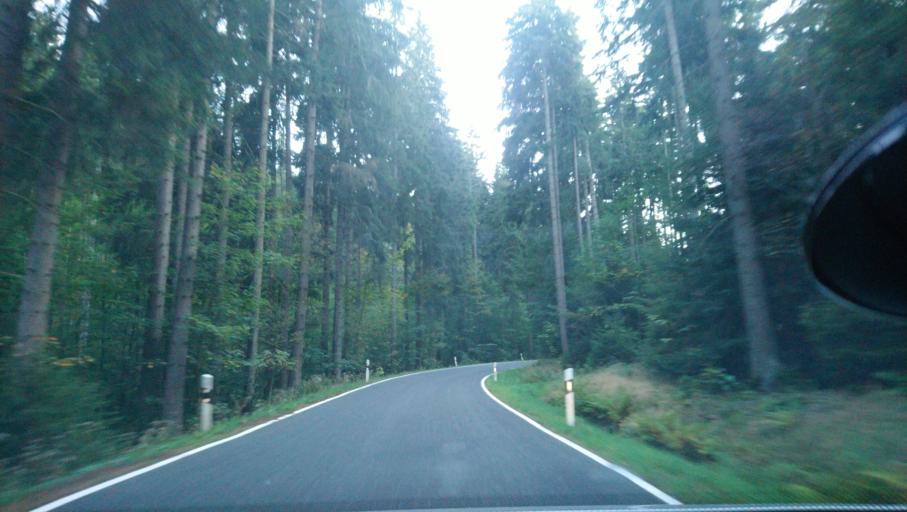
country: DE
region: Saxony
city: Barenstein
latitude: 50.5193
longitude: 13.0447
